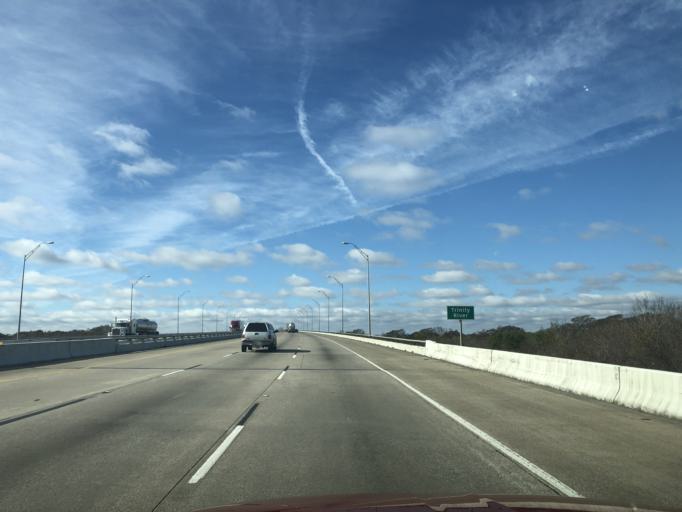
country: US
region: Texas
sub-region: Chambers County
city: Old River-Winfree
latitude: 29.8387
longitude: -94.7575
